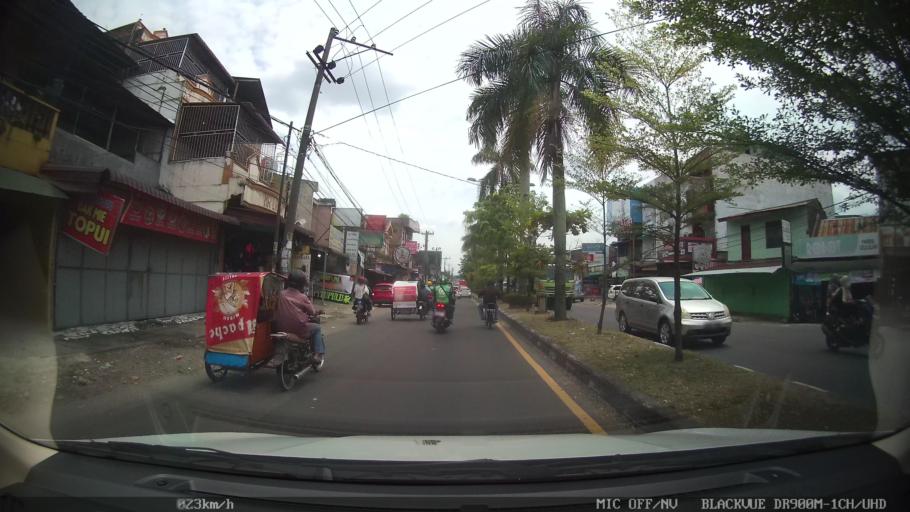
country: ID
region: North Sumatra
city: Deli Tua
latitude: 3.5379
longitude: 98.6517
